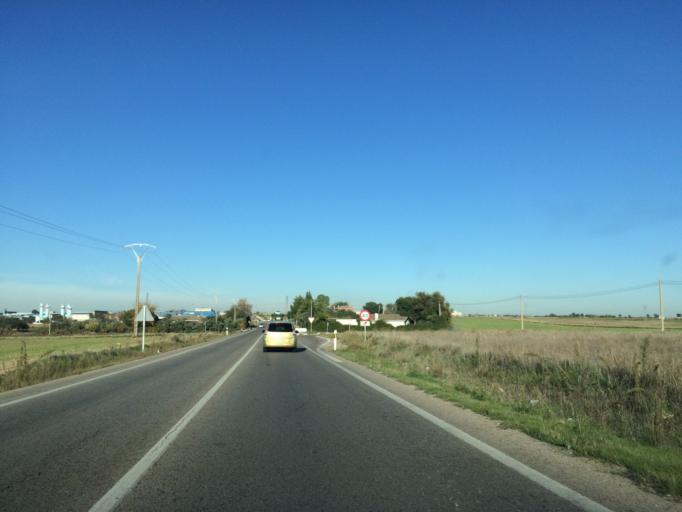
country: ES
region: Madrid
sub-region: Provincia de Madrid
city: Serranillos del Valle
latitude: 40.1908
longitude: -3.8774
